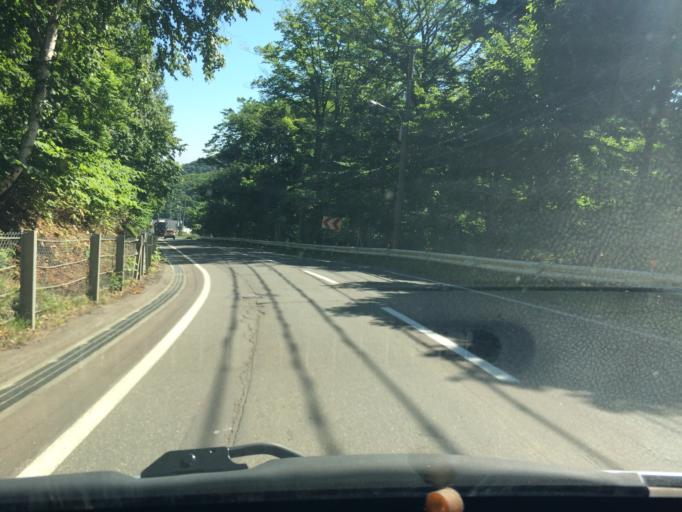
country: JP
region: Hokkaido
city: Sapporo
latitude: 43.0399
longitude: 141.2885
